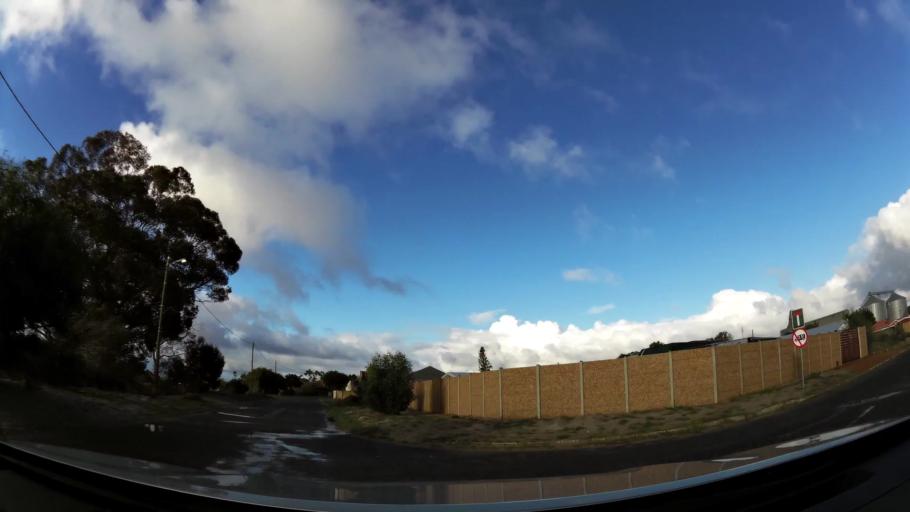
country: ZA
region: Western Cape
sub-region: Eden District Municipality
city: Riversdale
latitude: -34.2089
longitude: 21.5798
